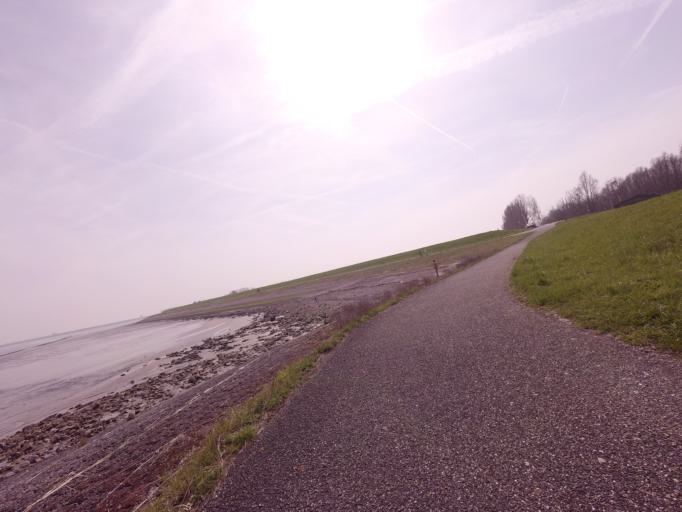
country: NL
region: Zeeland
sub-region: Gemeente Hulst
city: Hulst
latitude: 51.3803
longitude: 4.0365
